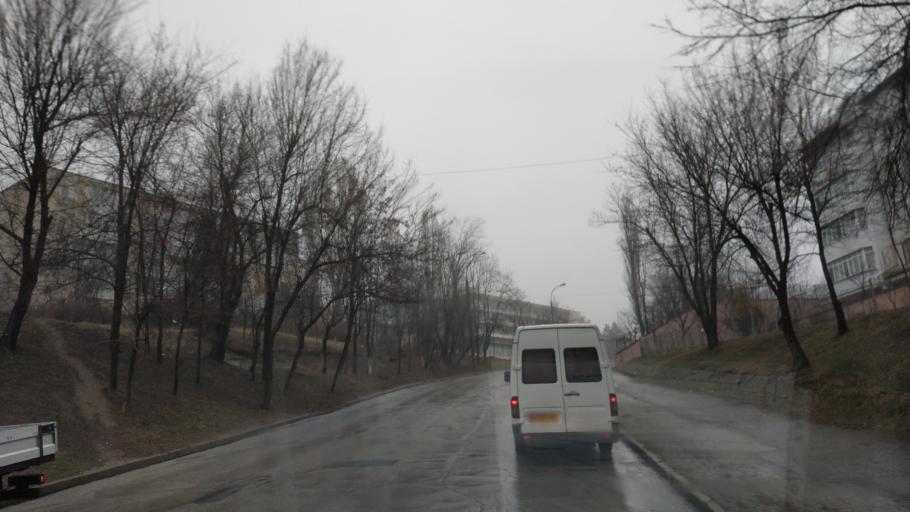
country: MD
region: Chisinau
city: Vatra
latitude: 47.0255
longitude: 28.7856
